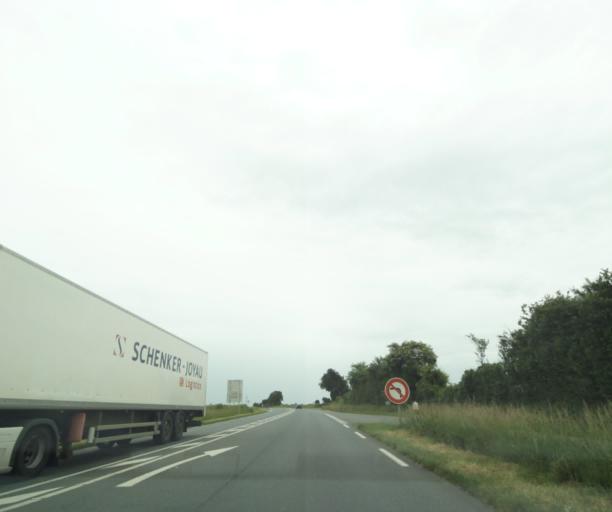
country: FR
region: Poitou-Charentes
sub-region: Departement des Deux-Sevres
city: Cherveux
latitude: 46.4307
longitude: -0.3916
